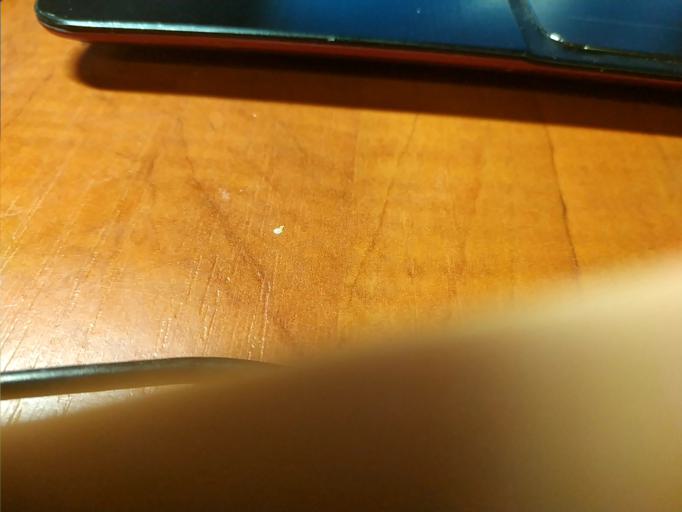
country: RU
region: Tverskaya
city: Likhoslavl'
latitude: 56.9845
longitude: 35.6196
